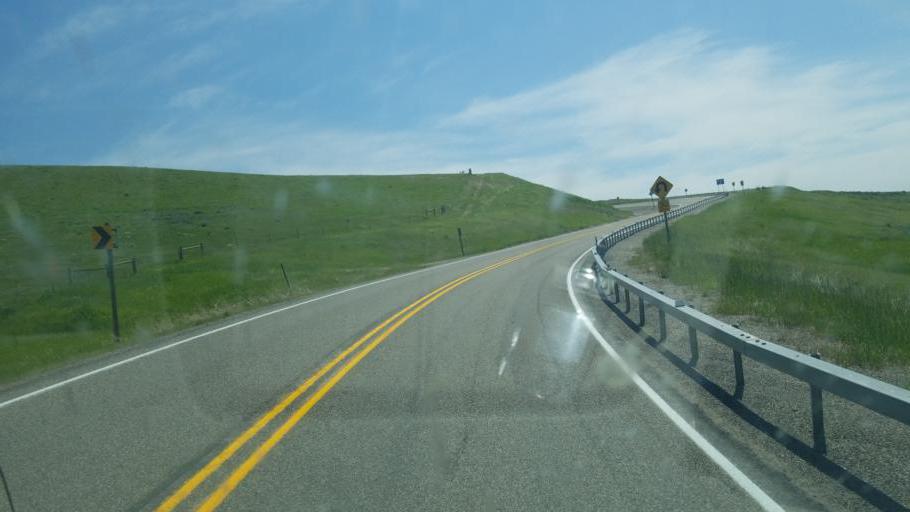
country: US
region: Montana
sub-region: Carbon County
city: Red Lodge
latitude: 45.1729
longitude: -109.2138
